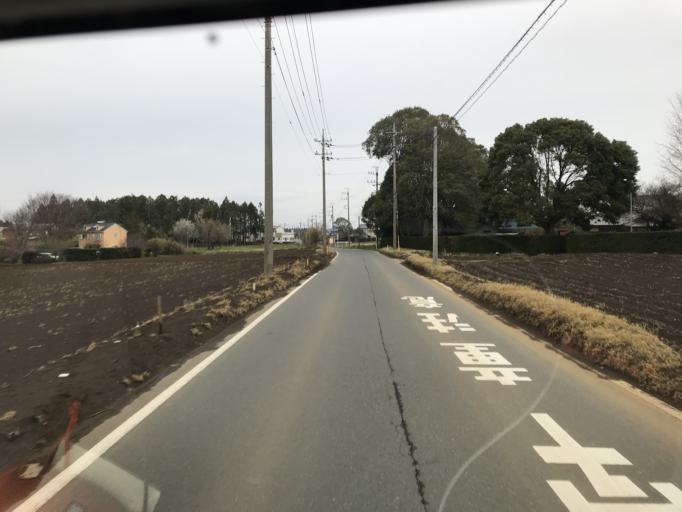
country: JP
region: Chiba
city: Sawara
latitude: 35.8485
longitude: 140.5142
